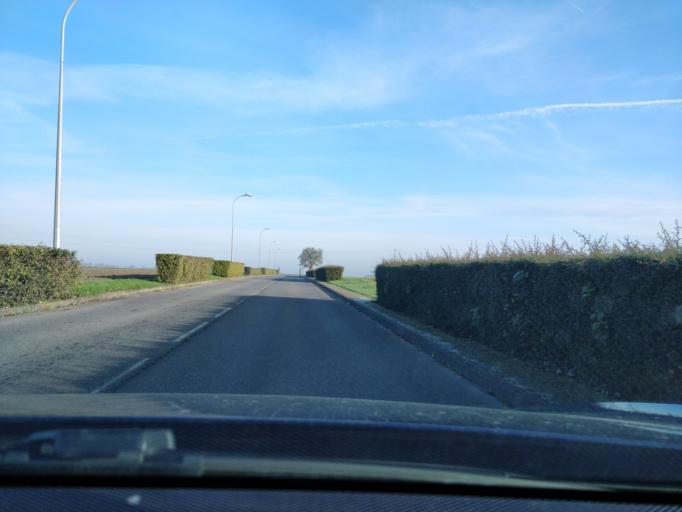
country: FR
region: Ile-de-France
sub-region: Departement de l'Essonne
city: Forges-les-Bains
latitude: 48.6495
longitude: 2.0979
